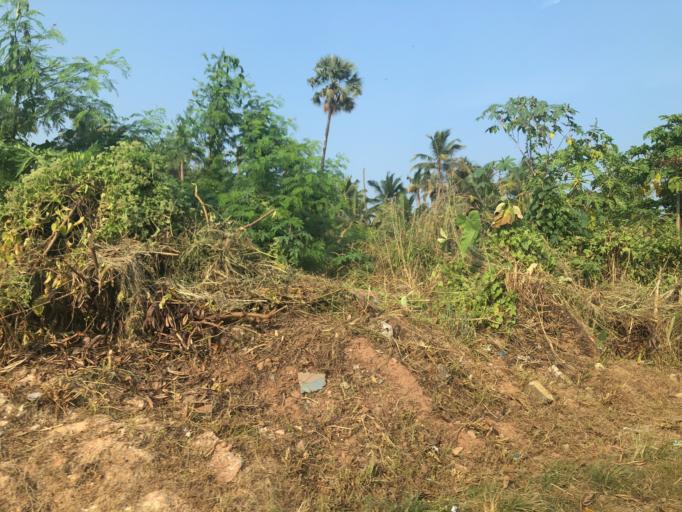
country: IN
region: Karnataka
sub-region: Dakshina Kannada
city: Ullal
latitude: 12.8147
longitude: 74.8545
